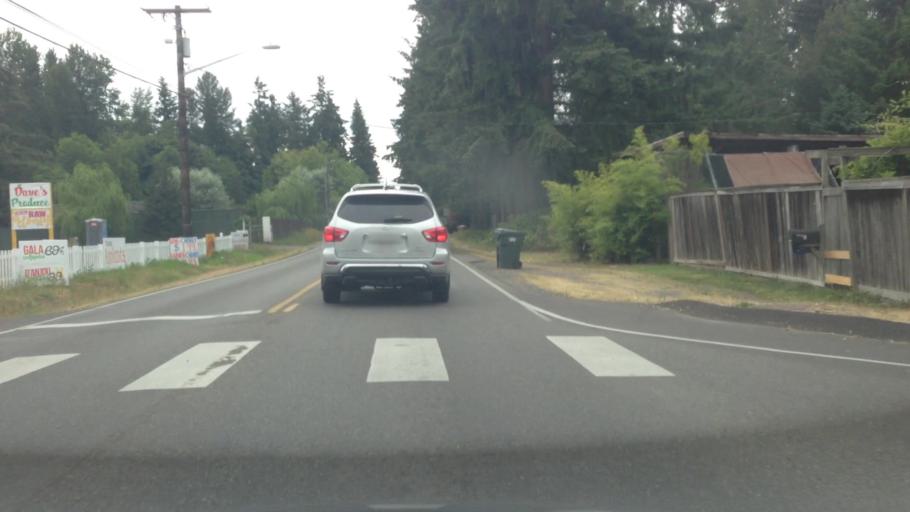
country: US
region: Washington
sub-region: Pierce County
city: South Hill
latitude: 47.1257
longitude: -122.3040
